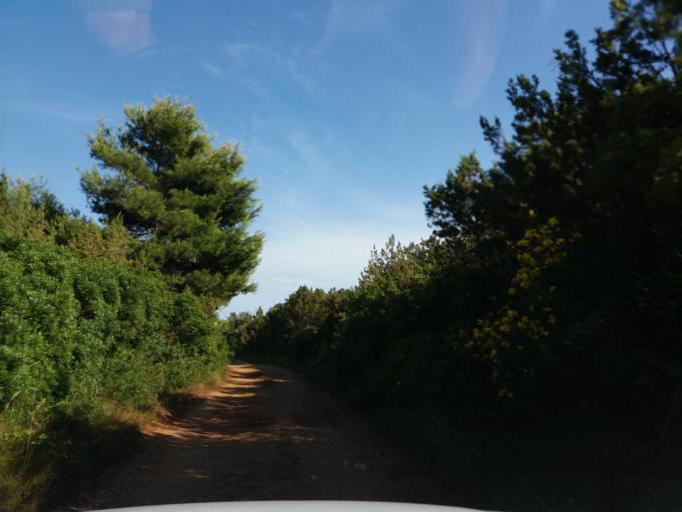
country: HR
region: Zadarska
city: Ugljan
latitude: 44.1320
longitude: 14.8622
